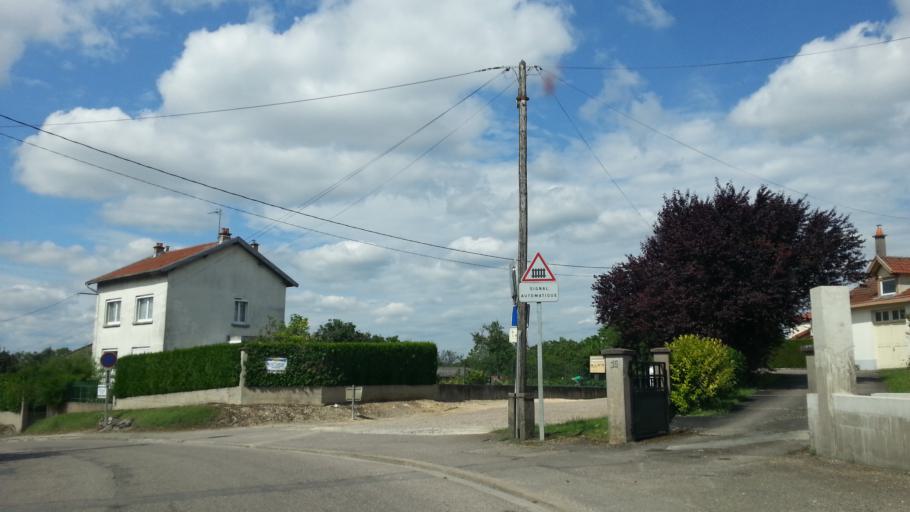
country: FR
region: Lorraine
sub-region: Departement de la Meuse
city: Thierville-sur-Meuse
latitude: 49.1564
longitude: 5.3660
